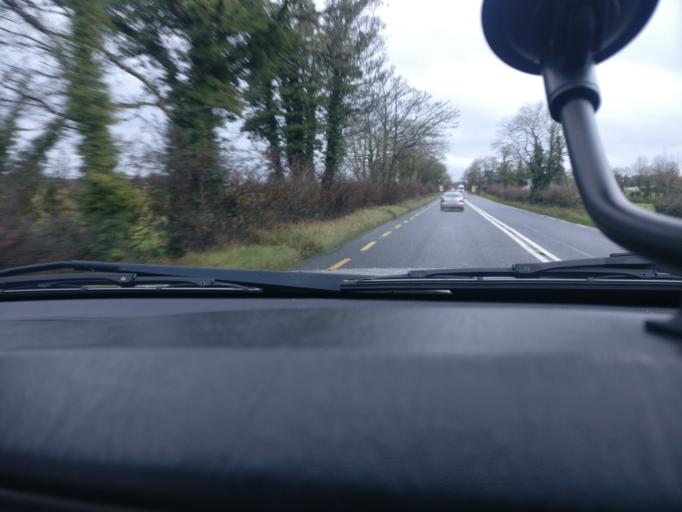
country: IE
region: Leinster
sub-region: An Mhi
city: Enfield
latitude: 53.4160
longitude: -6.7885
